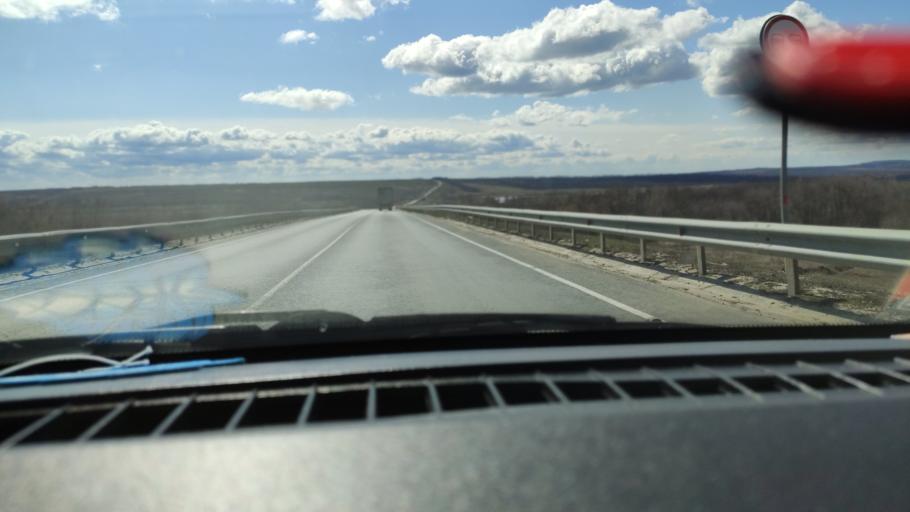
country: RU
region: Saratov
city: Dukhovnitskoye
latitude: 52.7488
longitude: 48.2497
